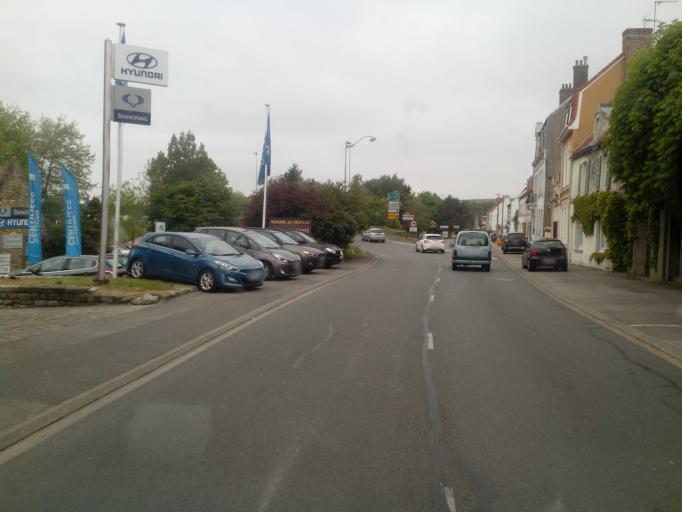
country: FR
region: Nord-Pas-de-Calais
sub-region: Departement du Pas-de-Calais
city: Saint-Leonard
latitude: 50.6857
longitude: 1.6273
